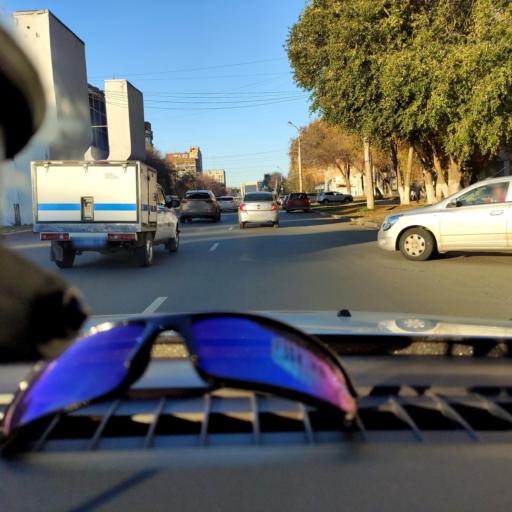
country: RU
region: Samara
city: Samara
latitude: 53.2003
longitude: 50.1745
